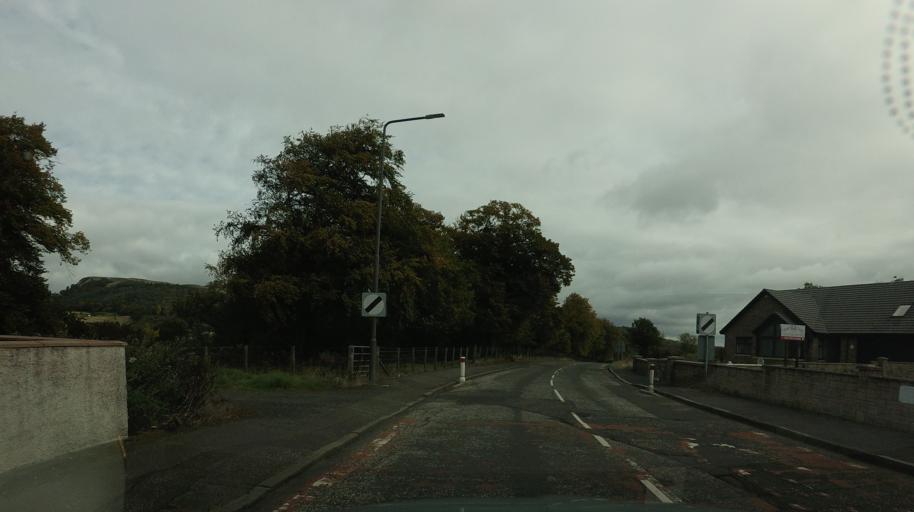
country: GB
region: Scotland
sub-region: Fife
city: Kelty
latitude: 56.1426
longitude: -3.3814
